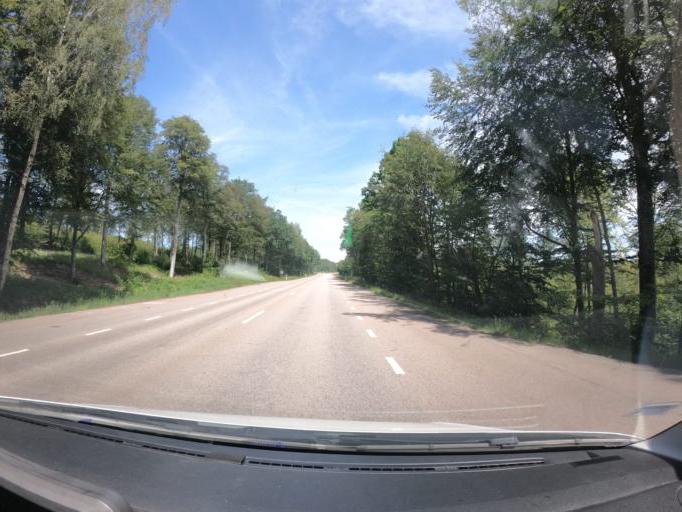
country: SE
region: Skane
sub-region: Orkelljunga Kommun
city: OErkelljunga
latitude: 56.2823
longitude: 13.2571
